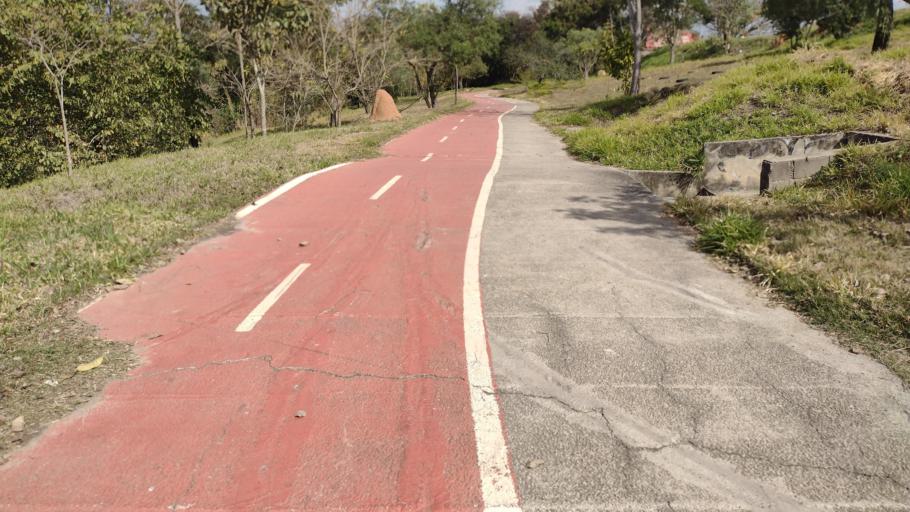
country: BR
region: Sao Paulo
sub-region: Sorocaba
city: Sorocaba
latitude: -23.4501
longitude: -47.4649
